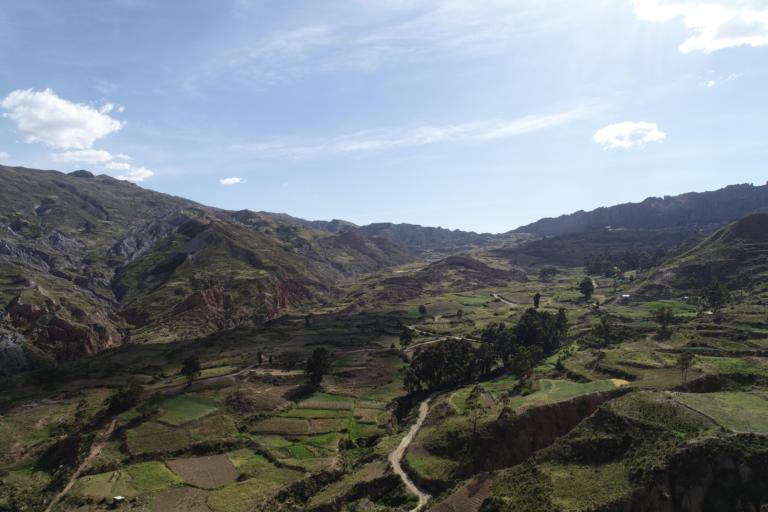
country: BO
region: La Paz
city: La Paz
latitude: -16.5552
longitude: -67.9829
